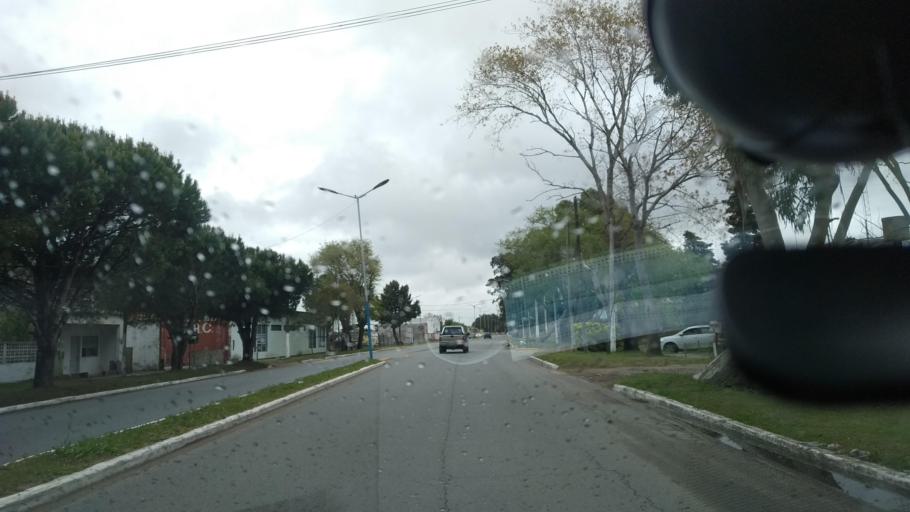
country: AR
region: Buenos Aires
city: San Clemente del Tuyu
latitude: -36.3821
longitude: -56.7227
